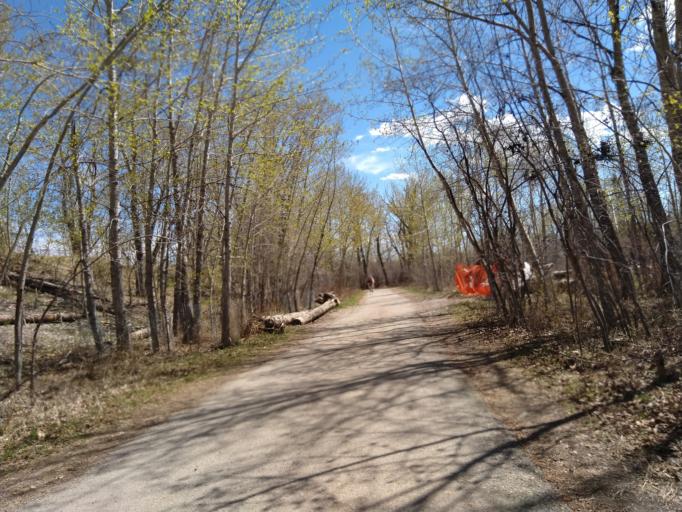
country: CA
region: Alberta
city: Calgary
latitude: 51.0996
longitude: -114.2084
